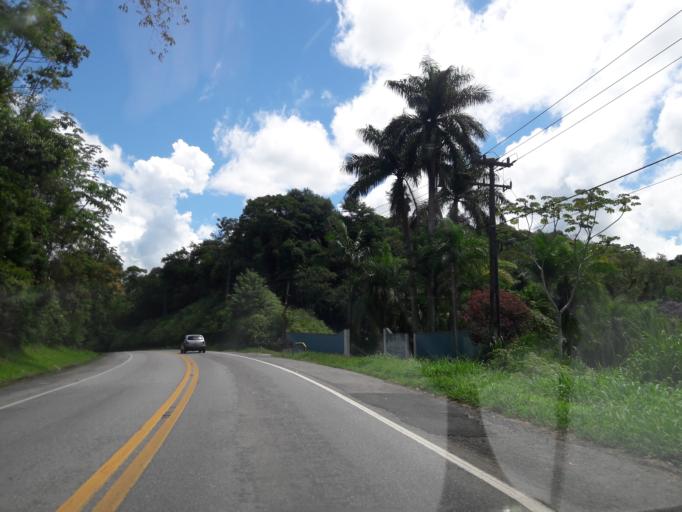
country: BR
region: Parana
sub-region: Antonina
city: Antonina
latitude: -25.4420
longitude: -48.7940
